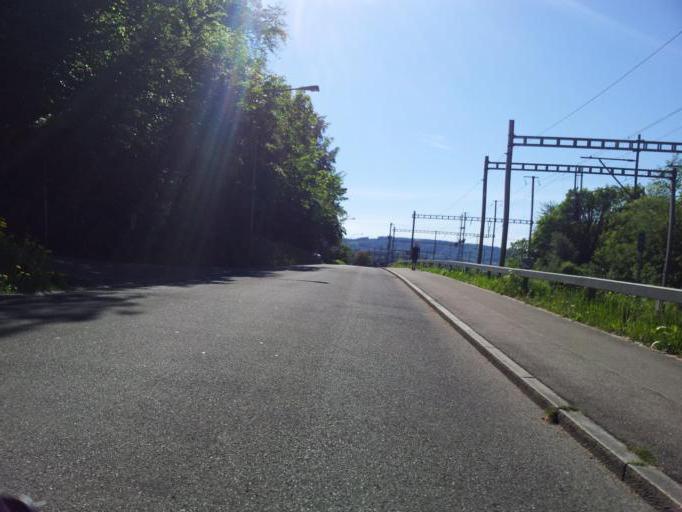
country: CH
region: Zurich
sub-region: Bezirk Dietikon
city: Schlieren / Freiestrasse
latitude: 47.3914
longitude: 8.4389
